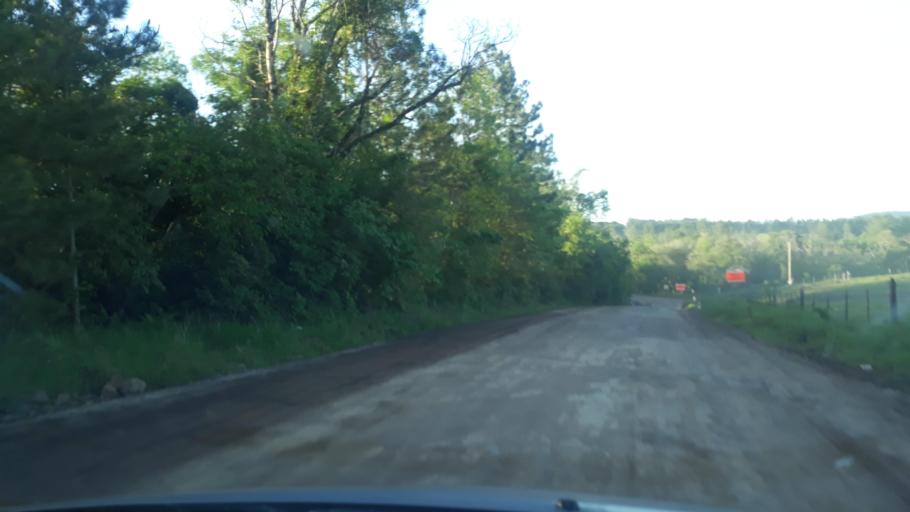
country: AR
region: Misiones
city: Ruiz de Montoya
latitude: -27.0472
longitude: -55.0038
